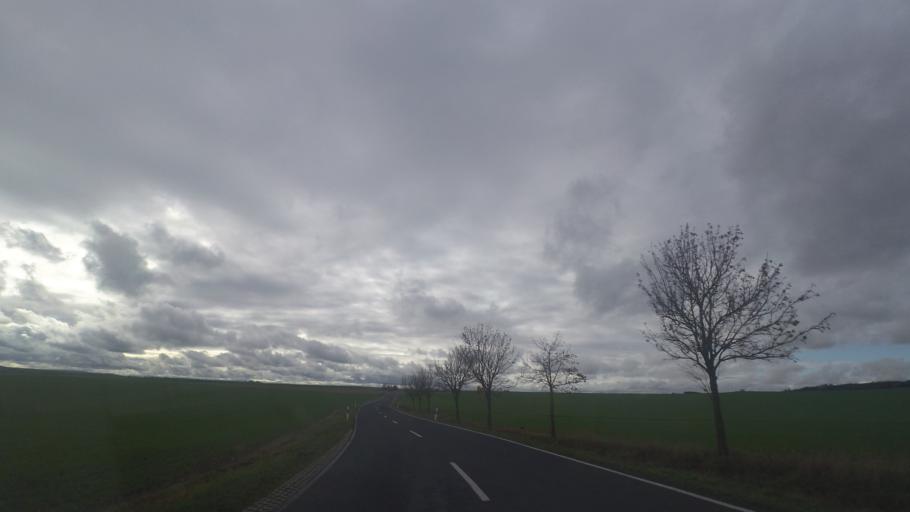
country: DE
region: Thuringia
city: Romhild
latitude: 50.3935
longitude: 10.5230
